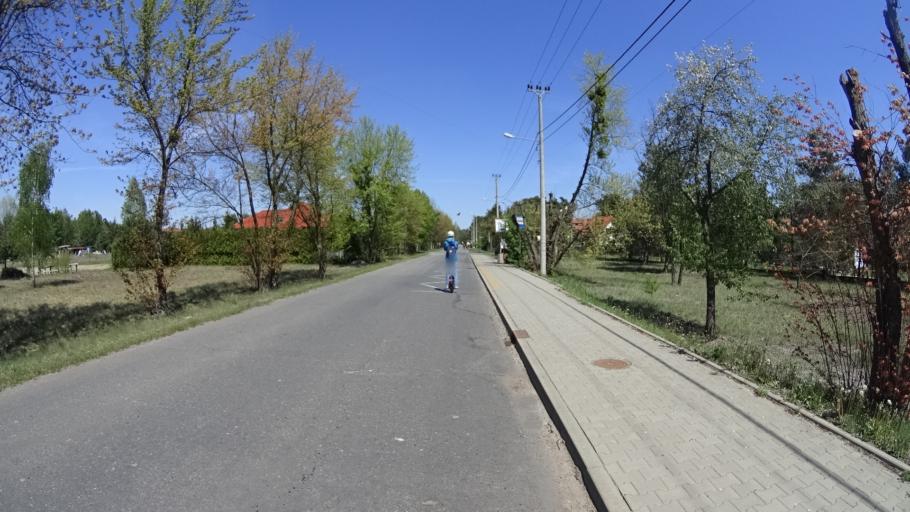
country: PL
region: Masovian Voivodeship
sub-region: Powiat warszawski zachodni
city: Truskaw
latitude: 52.2793
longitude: 20.7422
